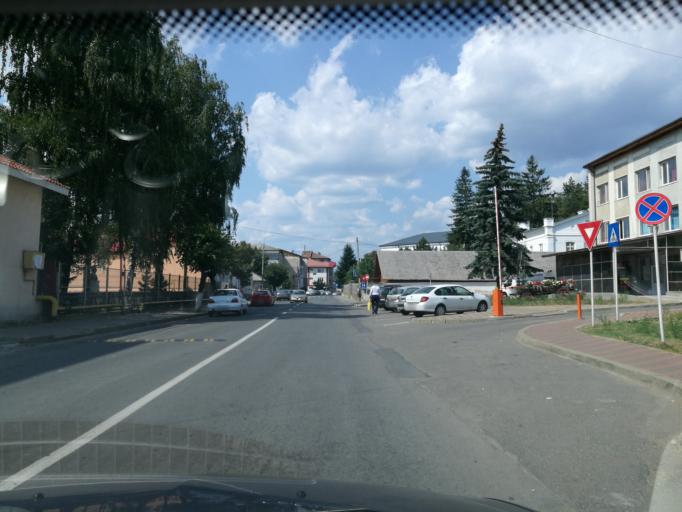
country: RO
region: Neamt
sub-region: Oras Targu Neamt
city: Targu Neamt
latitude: 47.2069
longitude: 26.3596
